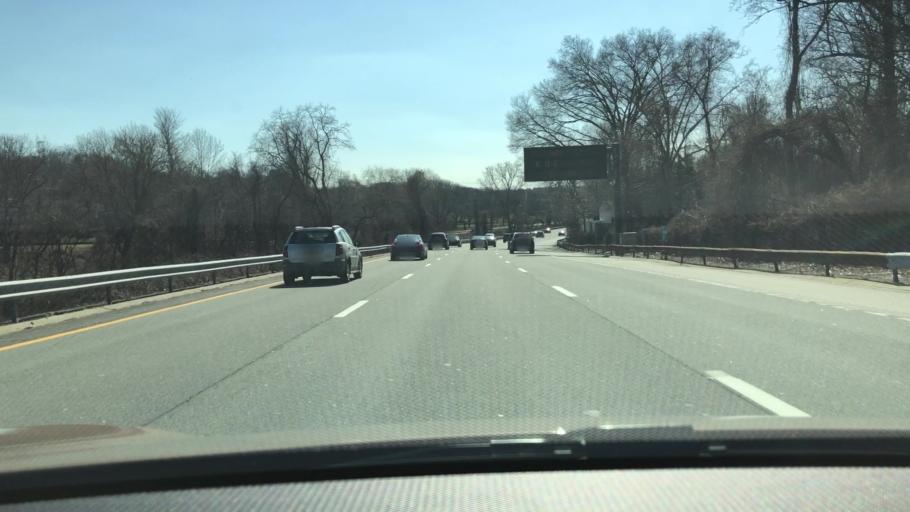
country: US
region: New York
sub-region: Westchester County
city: Tuckahoe
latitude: 40.9603
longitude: -73.8522
